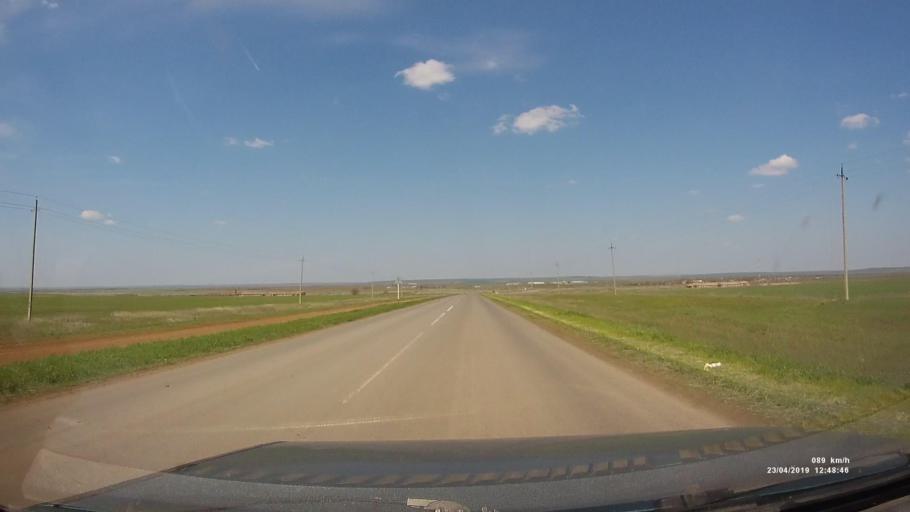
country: RU
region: Kalmykiya
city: Yashalta
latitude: 46.5289
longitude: 42.6389
